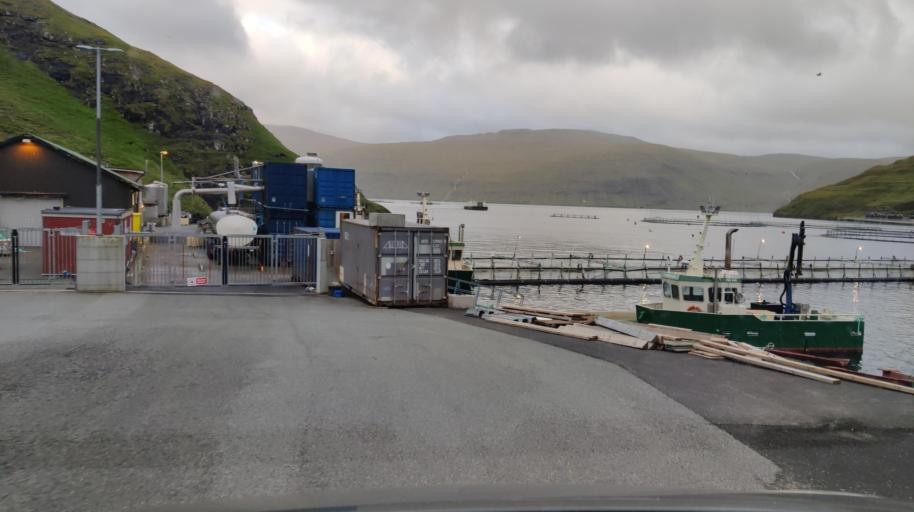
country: FO
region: Streymoy
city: Vestmanna
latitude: 62.1484
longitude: -7.1605
